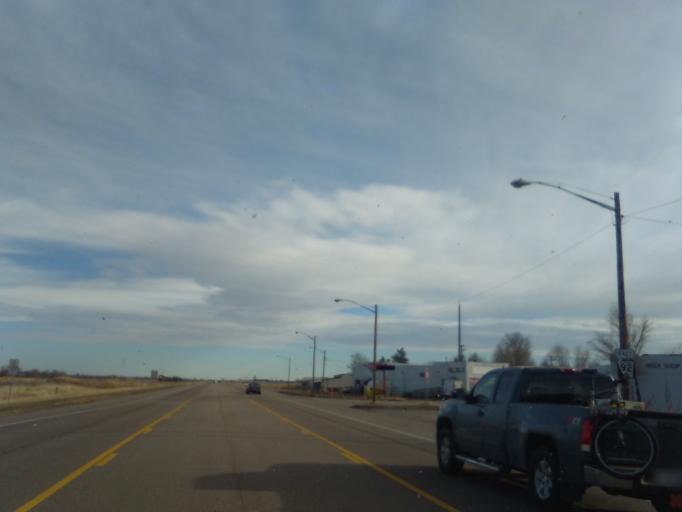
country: US
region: Nebraska
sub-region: Scotts Bluff County
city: Gering
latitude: 41.7838
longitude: -103.5174
